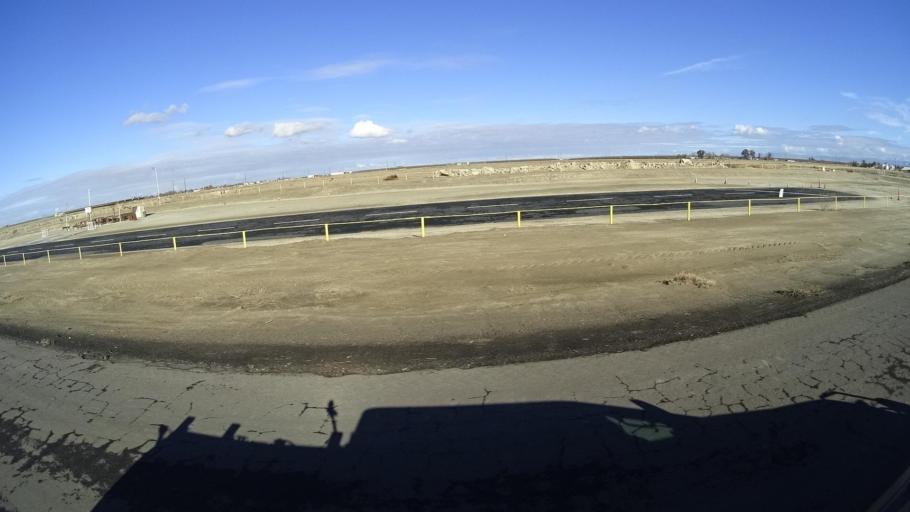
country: US
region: California
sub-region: Kern County
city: Rosedale
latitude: 35.3690
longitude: -119.2393
